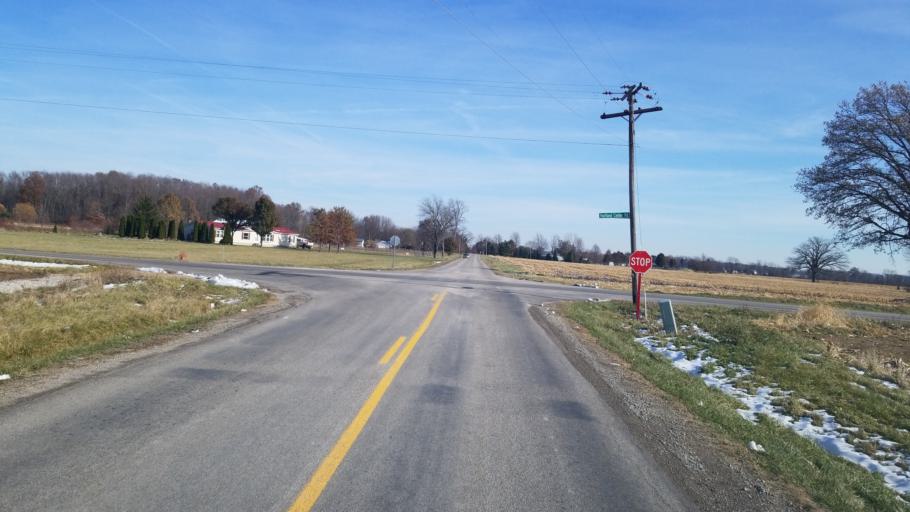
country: US
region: Ohio
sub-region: Huron County
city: Wakeman
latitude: 41.2035
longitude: -82.4920
